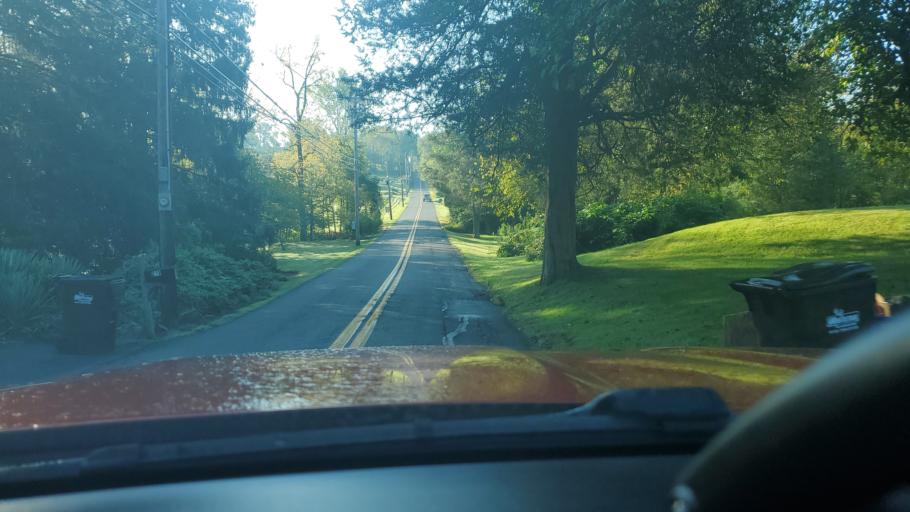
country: US
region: Pennsylvania
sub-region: Montgomery County
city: Woxall
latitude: 40.3040
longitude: -75.4792
